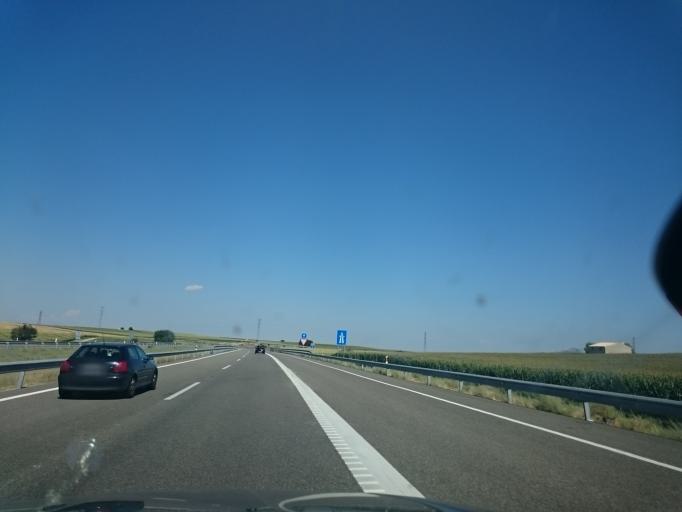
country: ES
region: Aragon
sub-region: Provincia de Huesca
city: Valfarta
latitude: 41.5177
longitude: -0.0948
